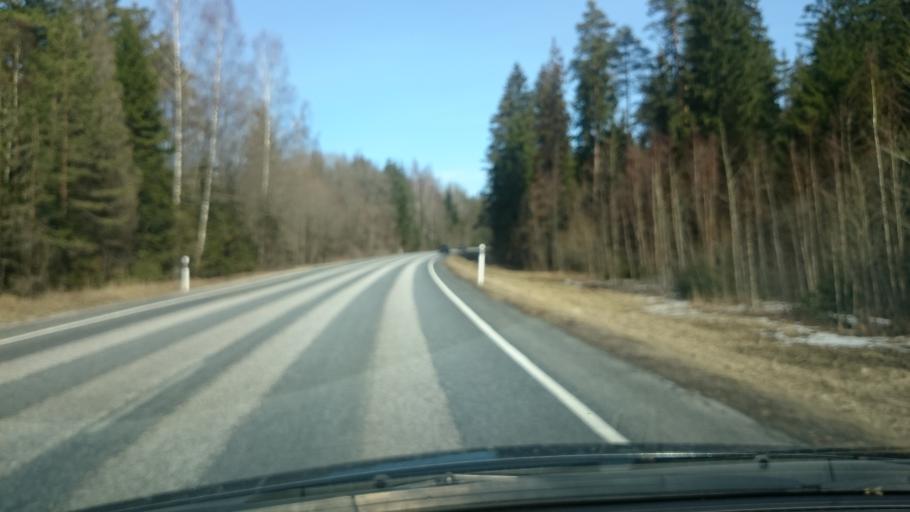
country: EE
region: Jaervamaa
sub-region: Tueri vald
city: Sarevere
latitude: 58.7405
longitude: 25.3025
